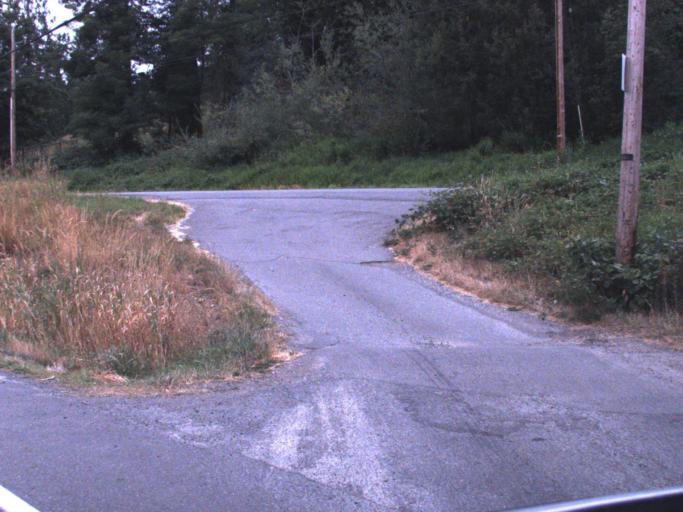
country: US
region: Washington
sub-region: King County
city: Fall City
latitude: 47.5803
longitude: -121.9380
